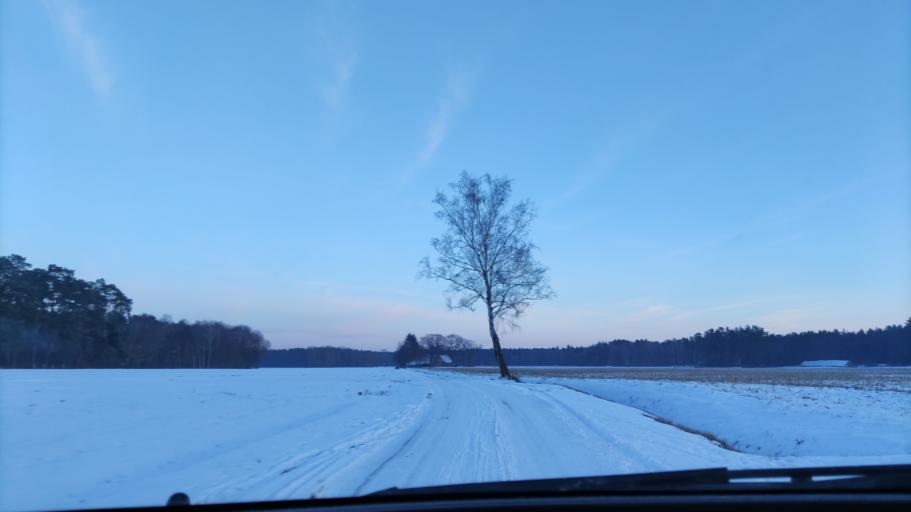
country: DE
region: Lower Saxony
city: Bleckede
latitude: 53.2924
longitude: 10.6758
